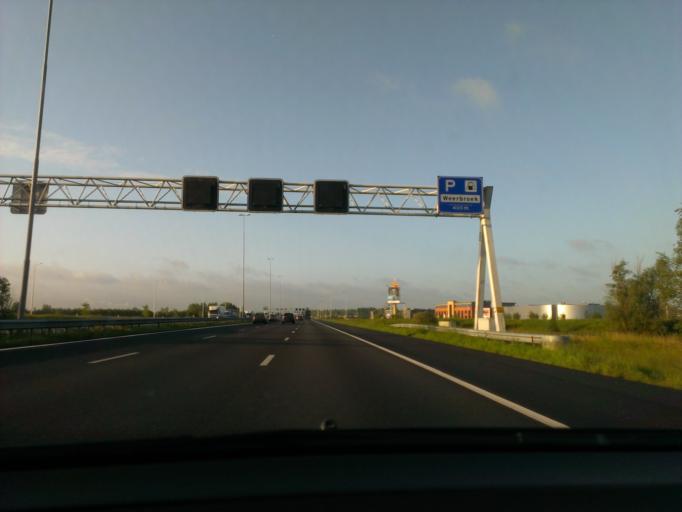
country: NL
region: Gelderland
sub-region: Gemeente Overbetuwe
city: Heteren
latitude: 51.9439
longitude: 5.7656
